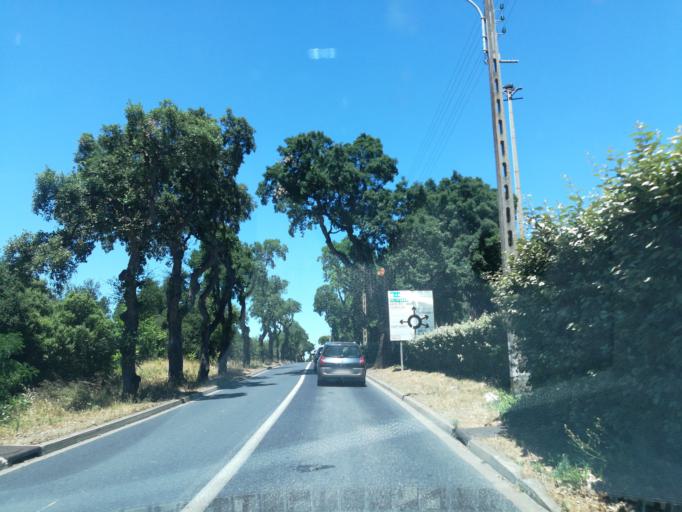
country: FR
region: Languedoc-Roussillon
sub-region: Departement des Pyrenees-Orientales
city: el Volo
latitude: 42.5116
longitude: 2.8289
